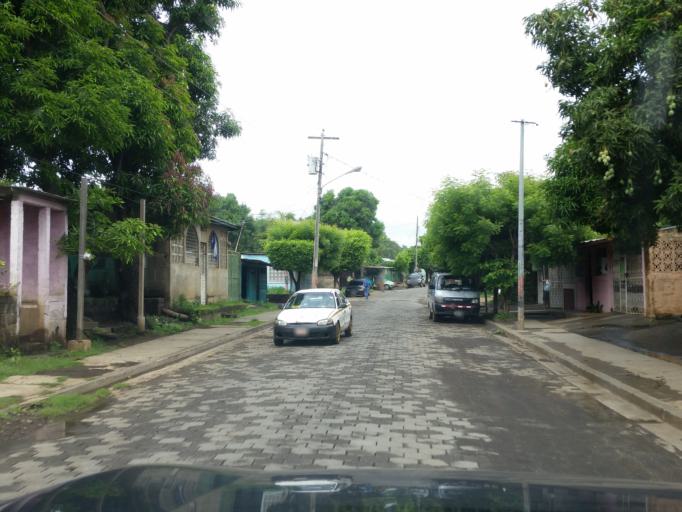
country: NI
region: Managua
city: Managua
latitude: 12.1034
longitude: -86.2214
